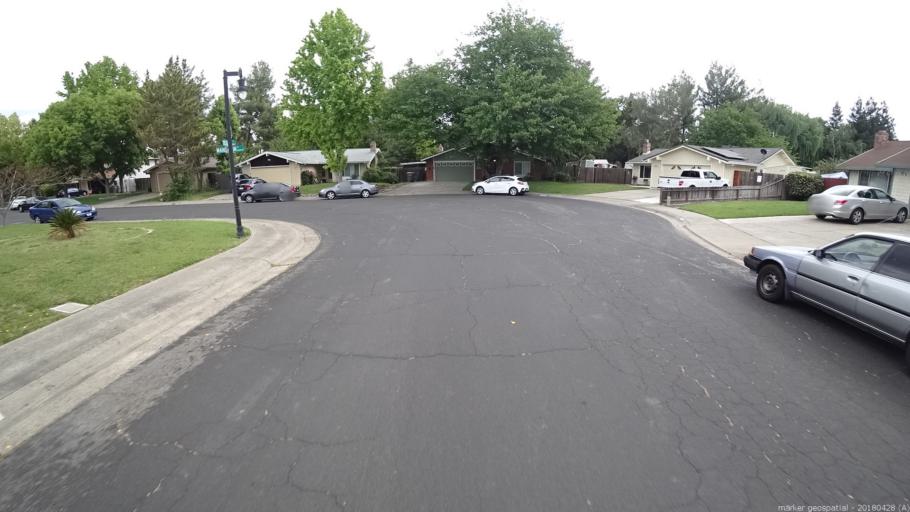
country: US
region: California
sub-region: Yolo County
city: West Sacramento
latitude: 38.5491
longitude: -121.5524
